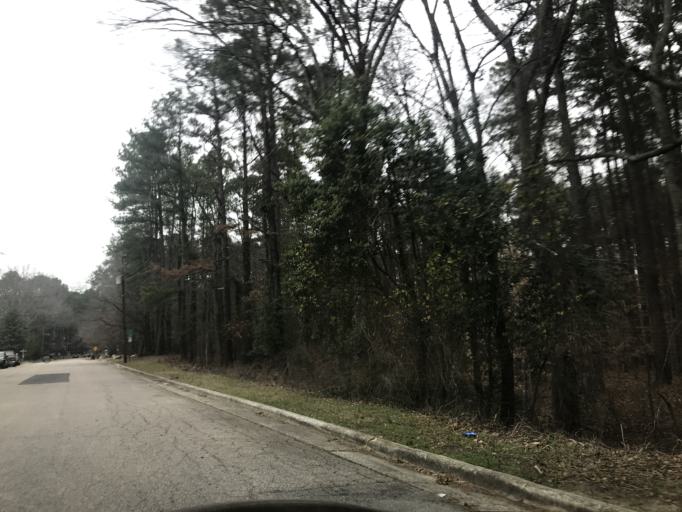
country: US
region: North Carolina
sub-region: Wake County
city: Raleigh
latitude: 35.7938
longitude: -78.5976
